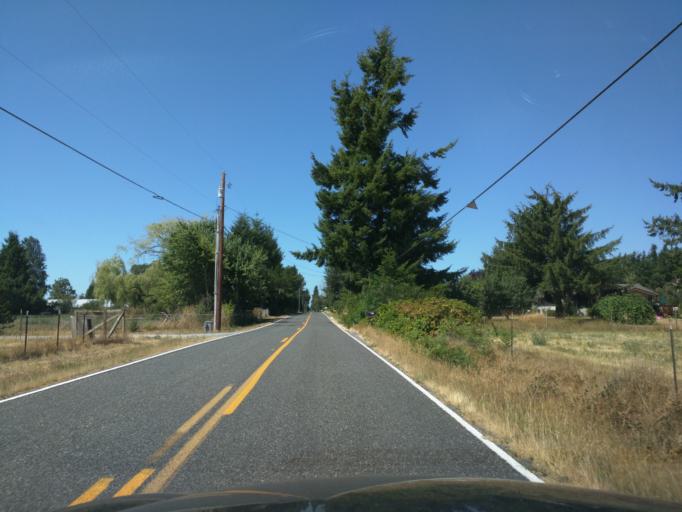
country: US
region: Washington
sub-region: Whatcom County
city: Lynden
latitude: 48.8772
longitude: -122.4170
